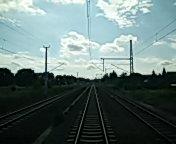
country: DE
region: Brandenburg
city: Halbe
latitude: 52.1112
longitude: 13.6987
